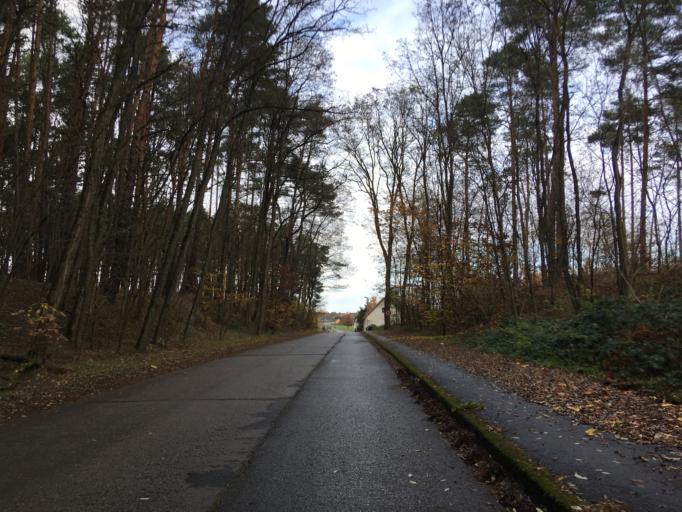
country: DE
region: Brandenburg
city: Schenkendobern
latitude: 51.9731
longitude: 14.5331
